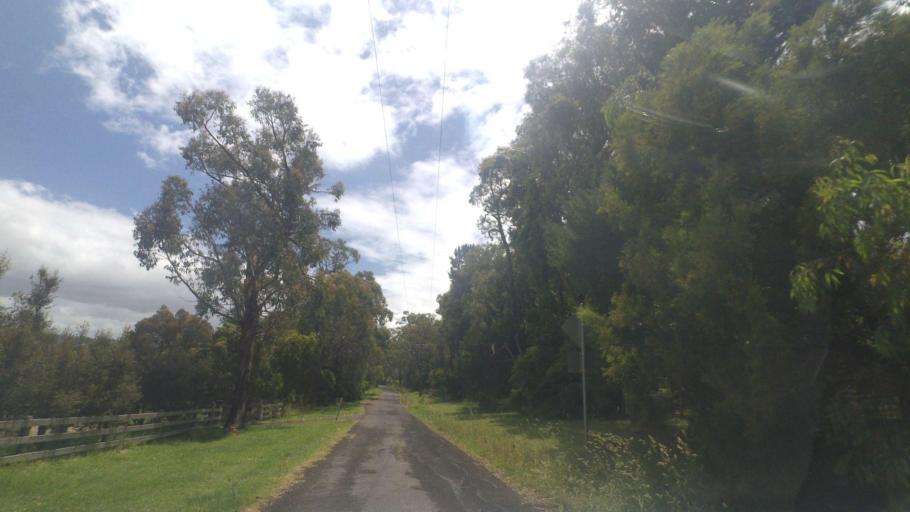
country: AU
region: Victoria
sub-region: Yarra Ranges
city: Mount Evelyn
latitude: -37.7752
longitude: 145.3744
